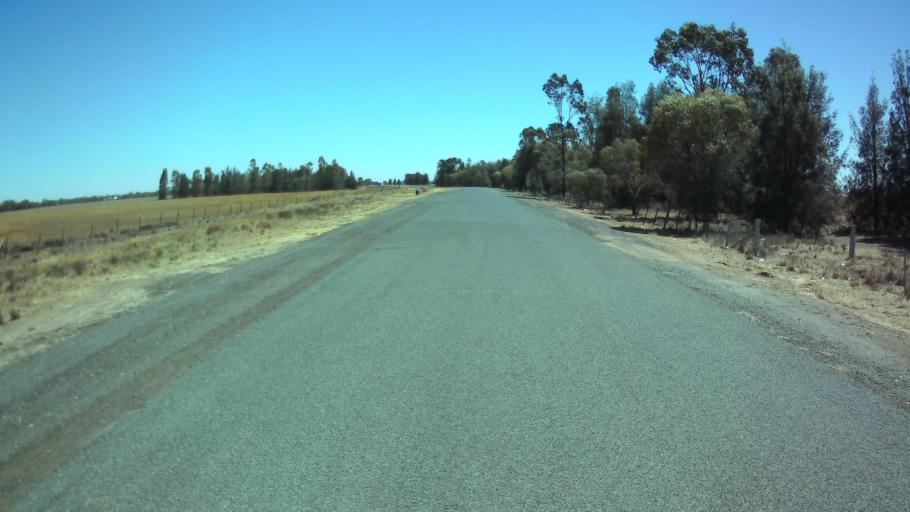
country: AU
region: New South Wales
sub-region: Bland
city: West Wyalong
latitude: -33.7584
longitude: 147.5278
